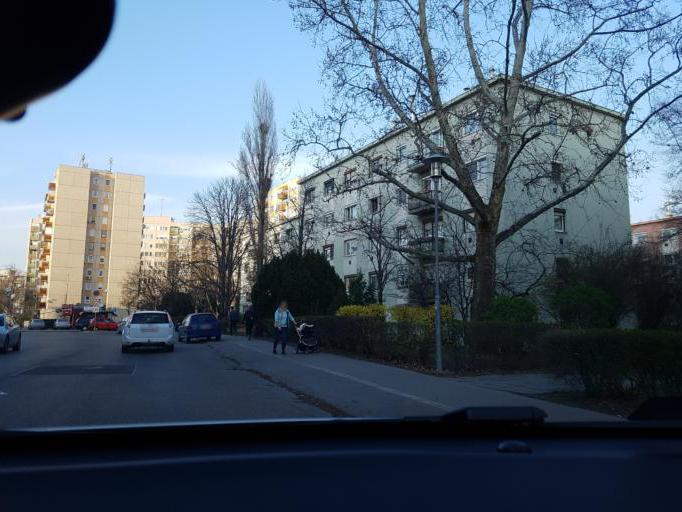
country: HU
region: Budapest
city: Budapest XX. keruelet
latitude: 47.4669
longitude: 19.1161
